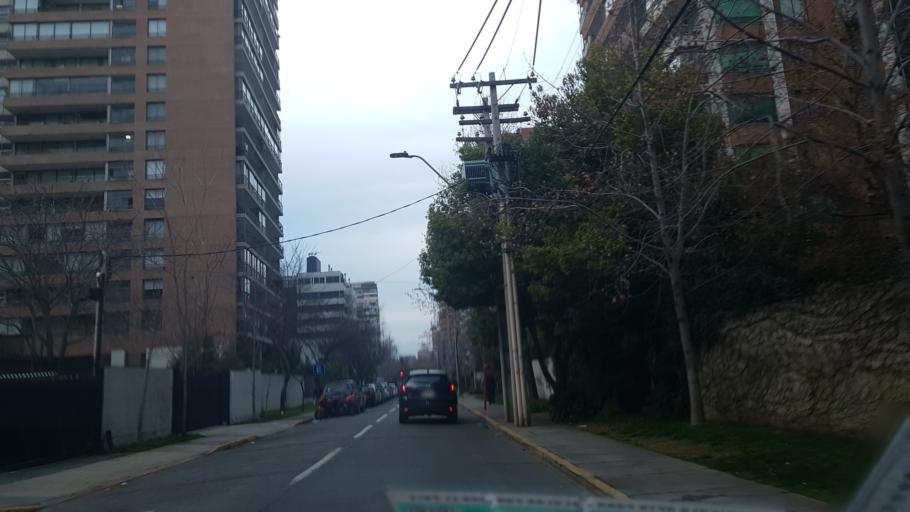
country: CL
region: Santiago Metropolitan
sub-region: Provincia de Santiago
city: Villa Presidente Frei, Nunoa, Santiago, Chile
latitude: -33.4099
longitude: -70.5779
